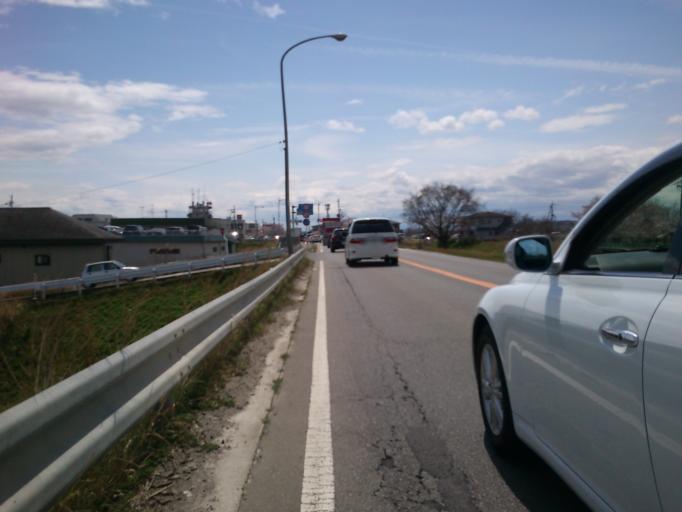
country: JP
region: Kyoto
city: Tanabe
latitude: 34.8006
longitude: 135.8031
